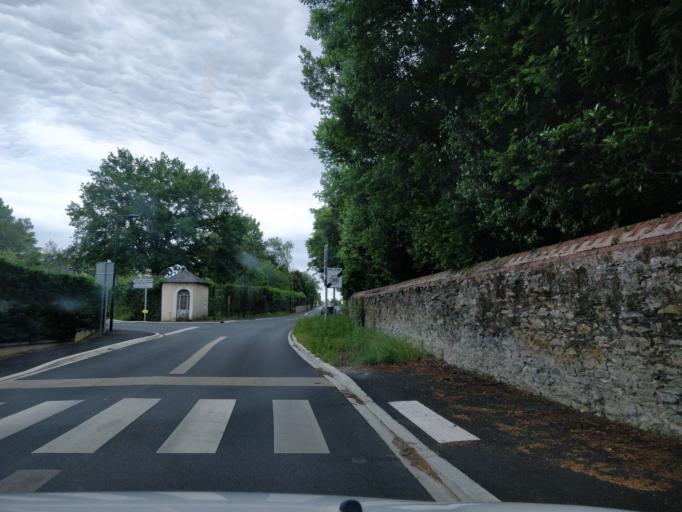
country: FR
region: Pays de la Loire
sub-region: Departement de Maine-et-Loire
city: Feneu
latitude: 47.5695
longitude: -0.5903
